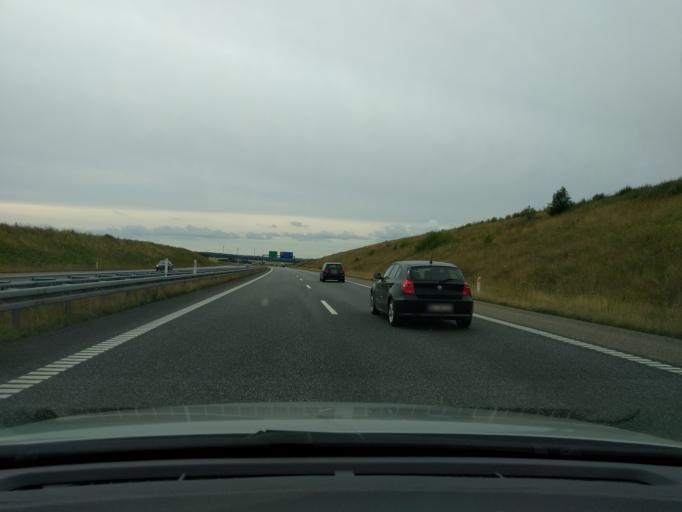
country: DK
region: Central Jutland
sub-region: Hedensted Kommune
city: Torring
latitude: 55.8280
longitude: 9.5273
